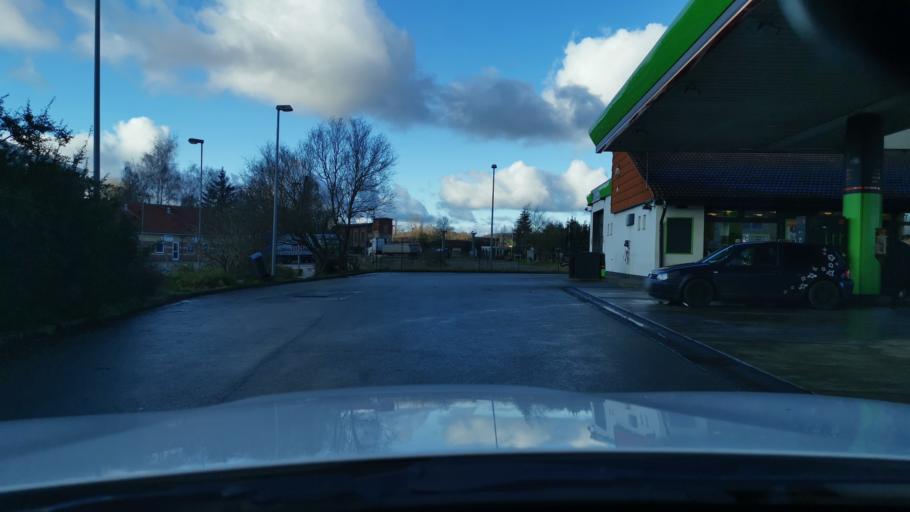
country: DE
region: Mecklenburg-Vorpommern
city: Tessin
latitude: 54.0305
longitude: 12.4701
